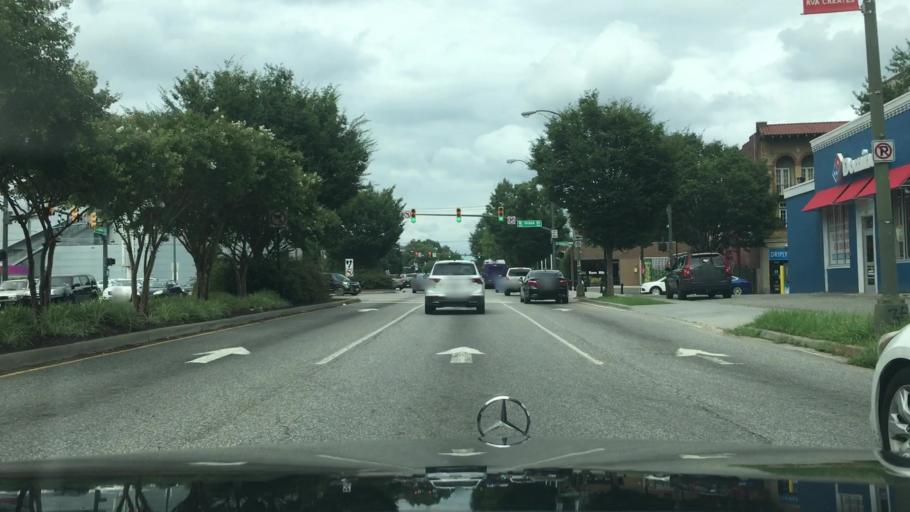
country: US
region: Virginia
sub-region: City of Richmond
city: Richmond
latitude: 37.5475
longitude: -77.4483
